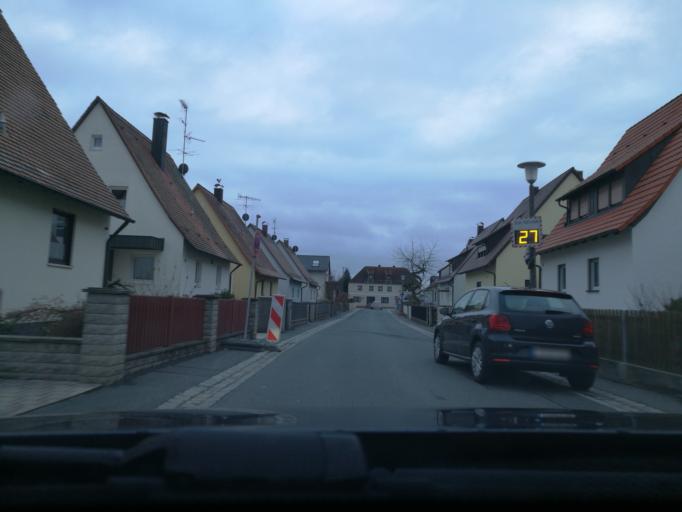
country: DE
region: Bavaria
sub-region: Regierungsbezirk Mittelfranken
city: Kalchreuth
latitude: 49.5585
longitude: 11.1377
